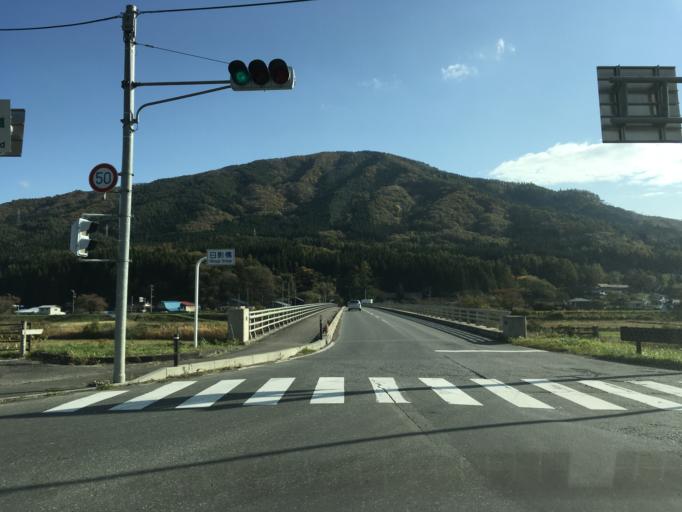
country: JP
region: Iwate
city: Tono
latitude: 39.3280
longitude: 141.4821
